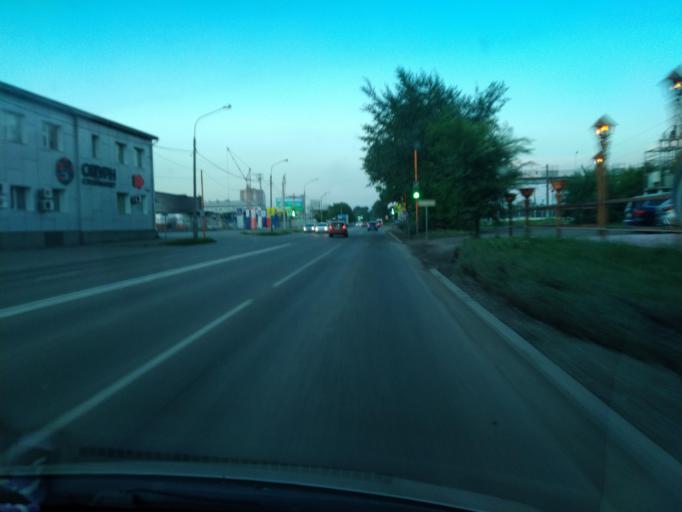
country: RU
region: Krasnoyarskiy
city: Krasnoyarsk
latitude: 55.9917
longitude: 92.9201
